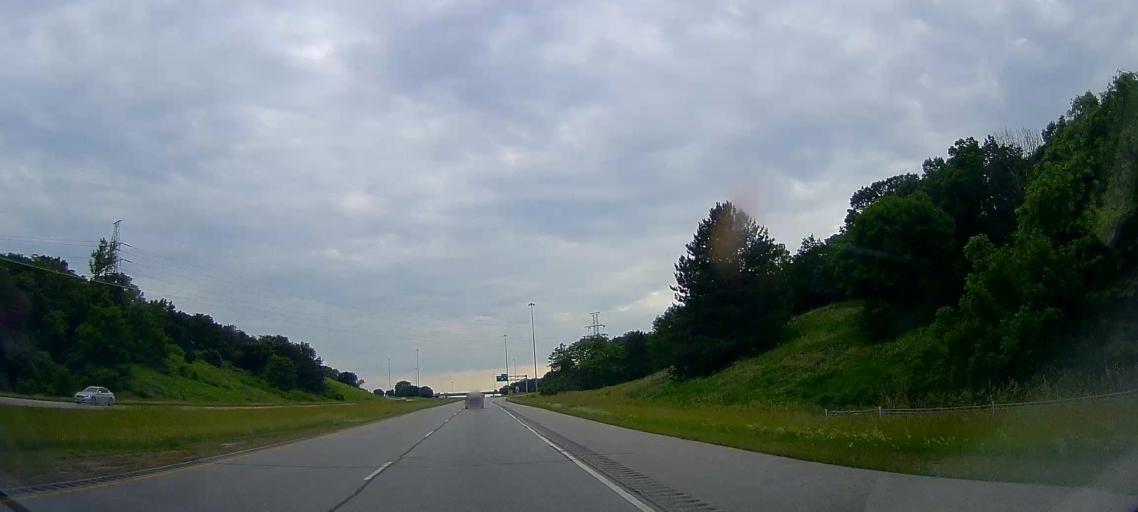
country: US
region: Iowa
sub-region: Pottawattamie County
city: Carter Lake
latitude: 41.3440
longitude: -96.0163
